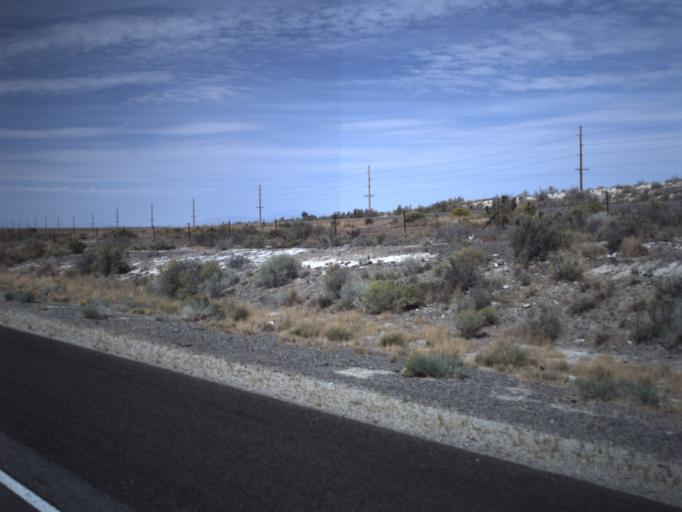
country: US
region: Utah
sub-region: Tooele County
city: Grantsville
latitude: 40.7266
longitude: -113.1363
